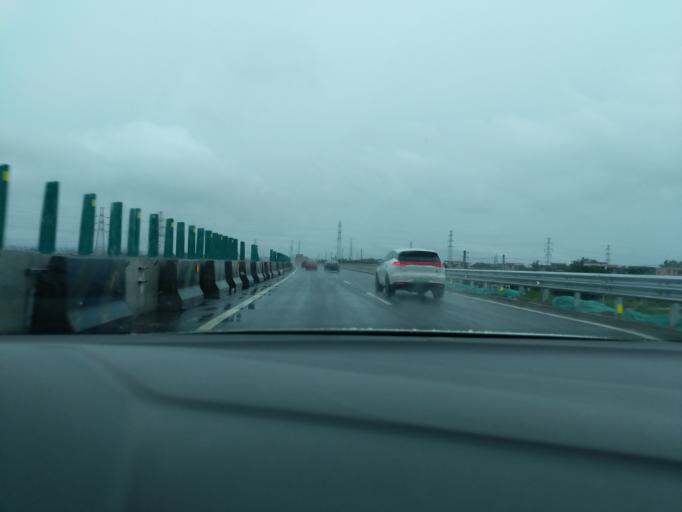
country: CN
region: Guangdong
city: Shuikou
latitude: 22.4661
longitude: 112.7519
